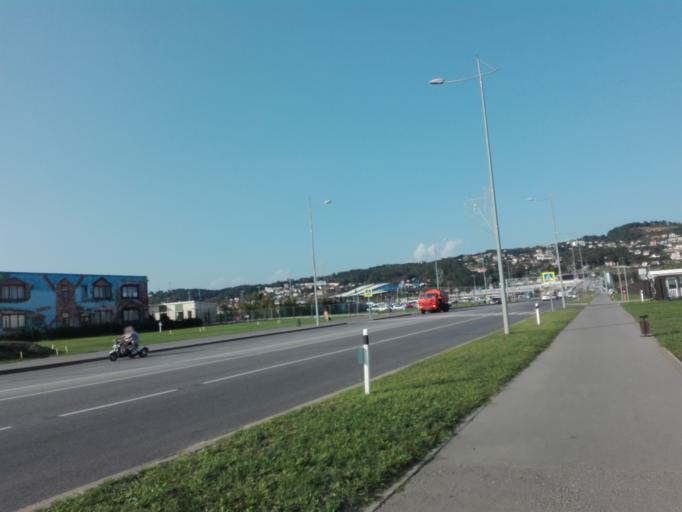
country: RU
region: Krasnodarskiy
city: Adler
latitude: 43.4044
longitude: 39.9717
